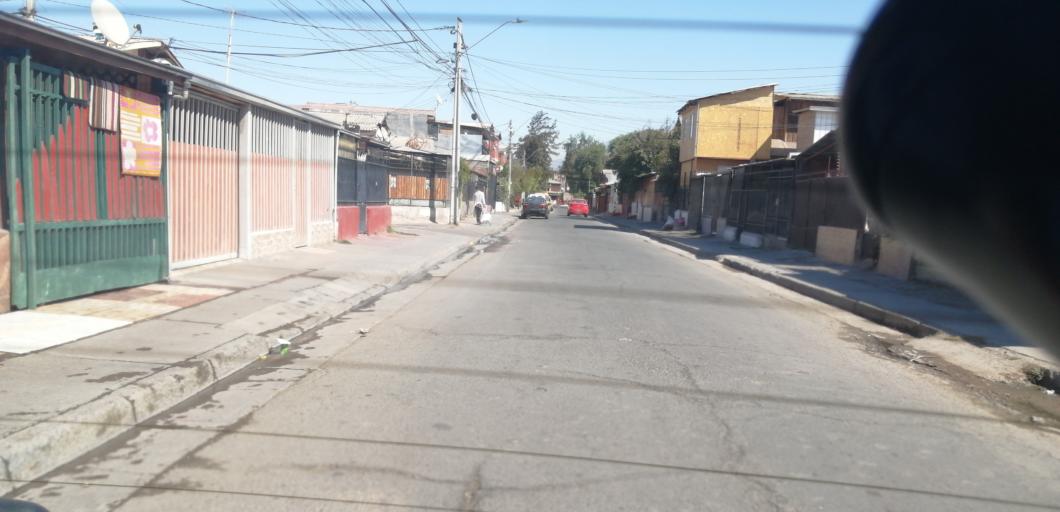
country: CL
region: Santiago Metropolitan
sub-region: Provincia de Santiago
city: Lo Prado
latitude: -33.4443
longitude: -70.7615
